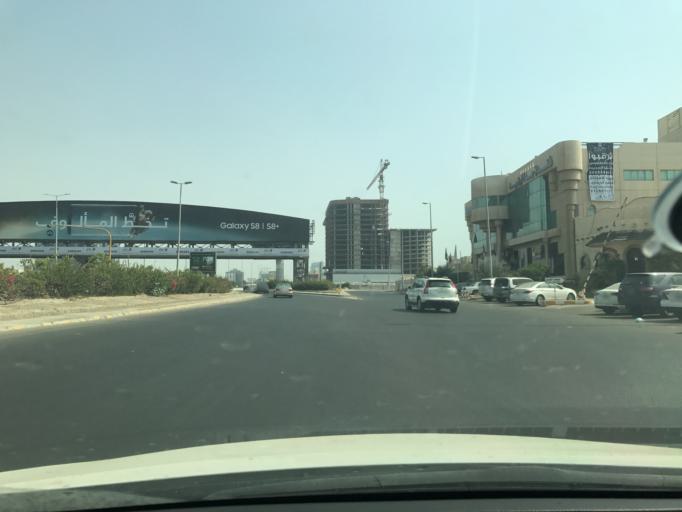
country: SA
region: Makkah
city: Jeddah
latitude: 21.6239
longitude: 39.1534
